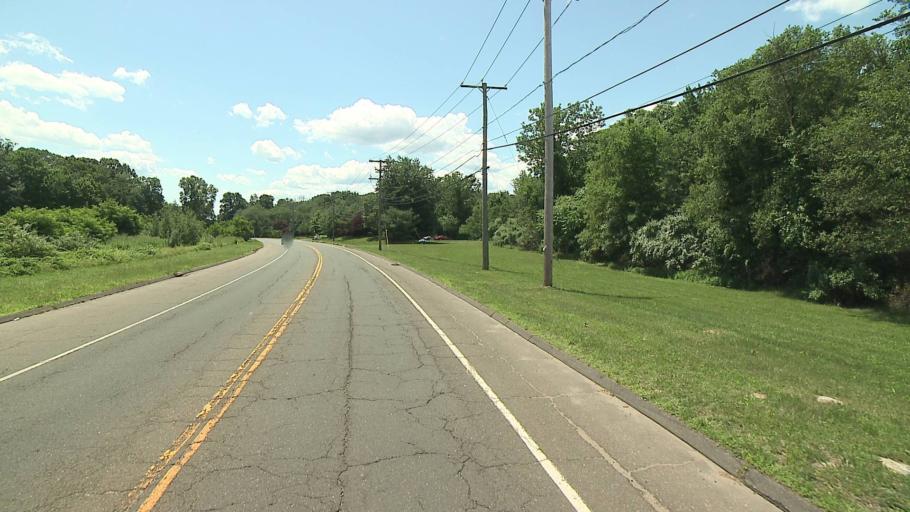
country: US
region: Connecticut
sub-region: Fairfield County
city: Trumbull
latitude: 41.2255
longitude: -73.1658
